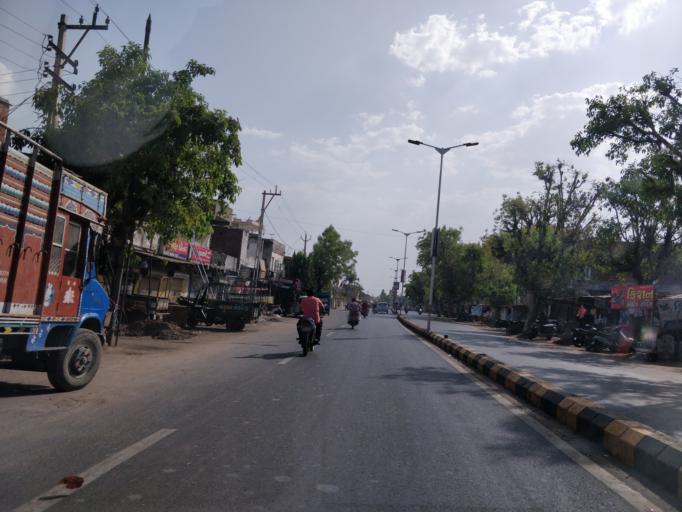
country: IN
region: Gujarat
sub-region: Ahmadabad
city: Naroda
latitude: 23.0766
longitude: 72.6625
